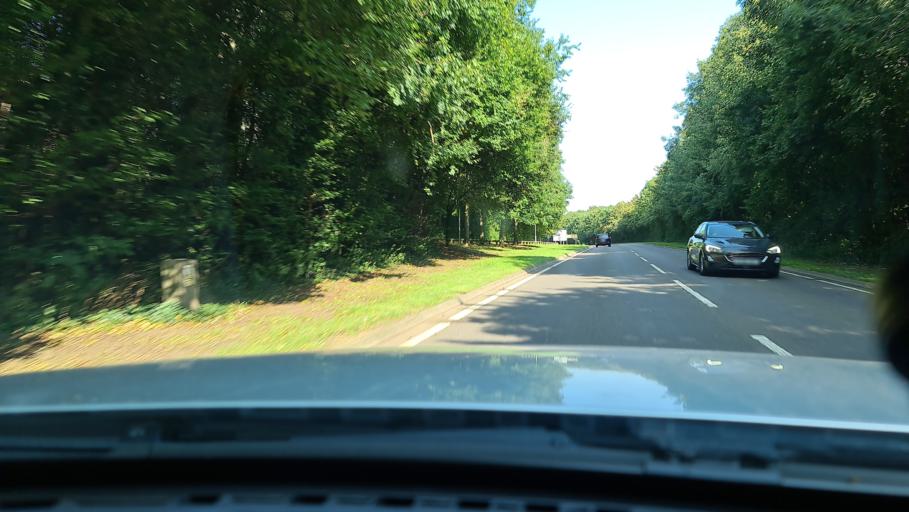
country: GB
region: England
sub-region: Northamptonshire
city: Daventry
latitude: 52.2699
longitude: -1.1588
